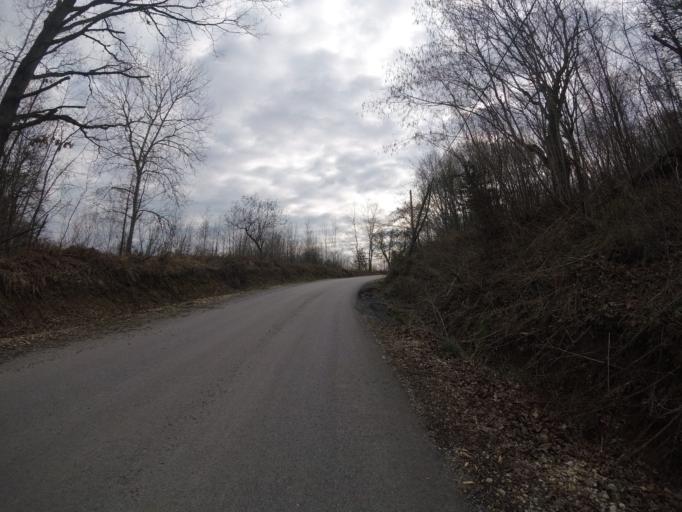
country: HR
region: Sisacko-Moslavacka
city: Glina
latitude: 45.4369
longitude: 16.0764
